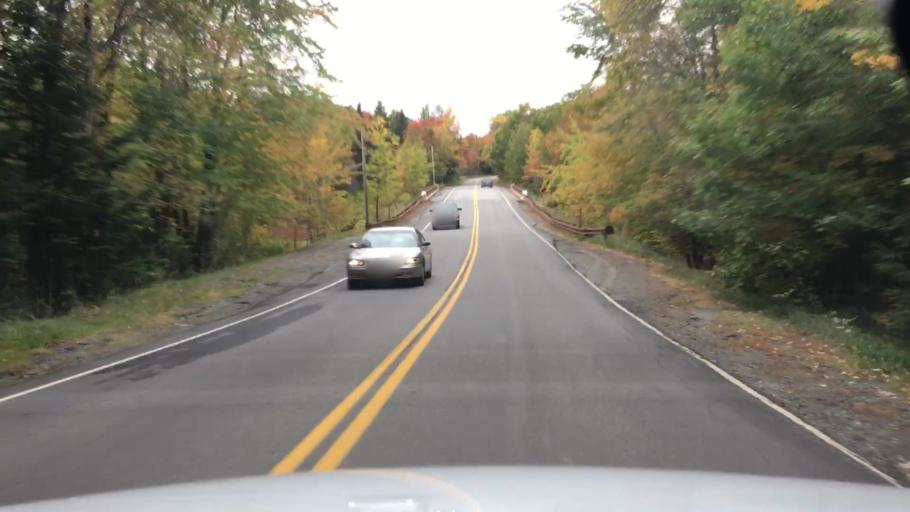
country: US
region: Maine
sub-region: Penobscot County
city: Hudson
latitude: 44.9850
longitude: -68.7918
